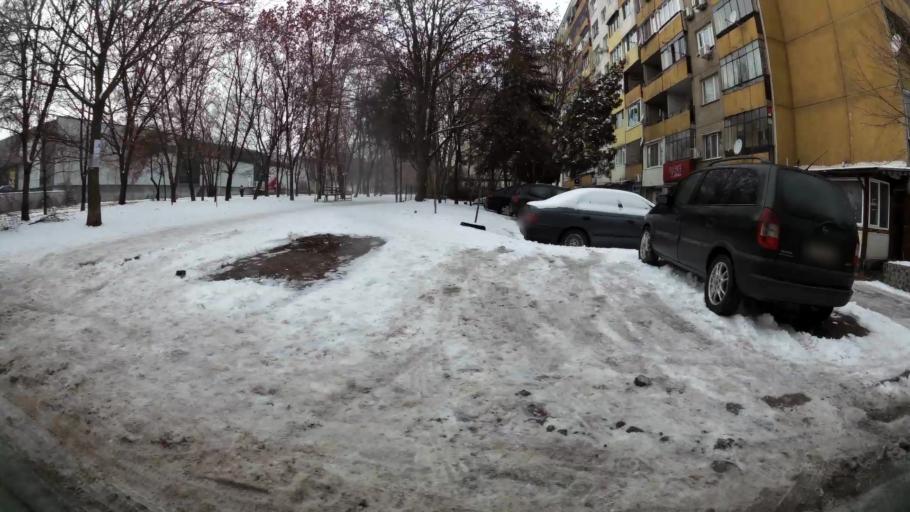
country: BG
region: Sofia-Capital
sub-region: Stolichna Obshtina
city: Sofia
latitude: 42.7126
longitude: 23.3024
